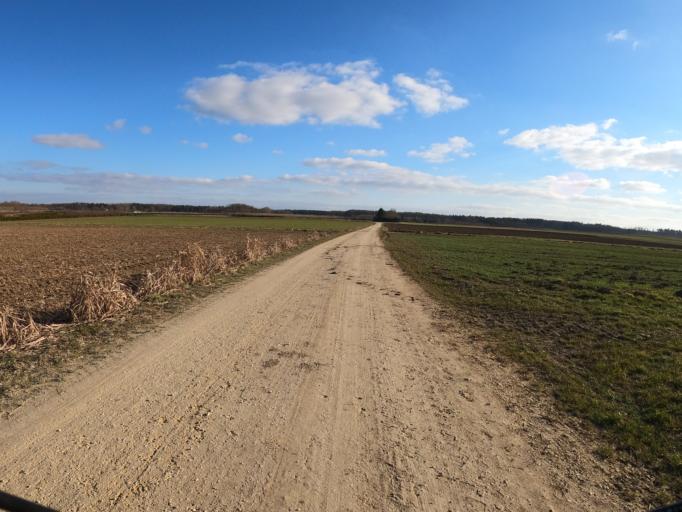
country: DE
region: Bavaria
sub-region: Swabia
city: Leipheim
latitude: 48.4344
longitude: 10.2133
